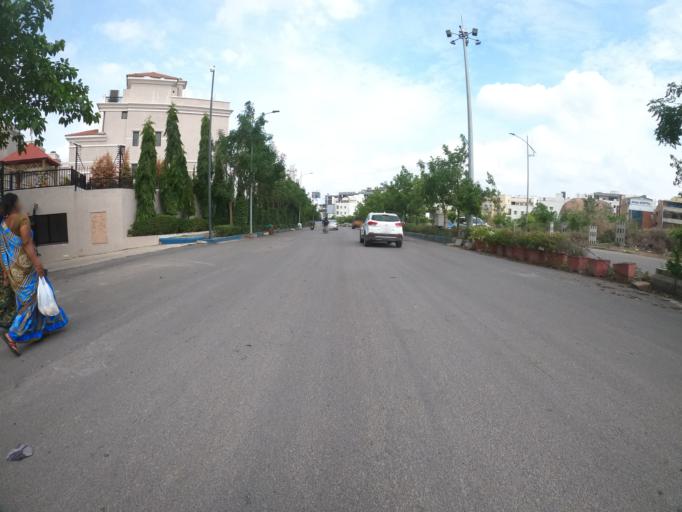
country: IN
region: Telangana
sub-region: Hyderabad
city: Hyderabad
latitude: 17.4078
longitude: 78.3739
